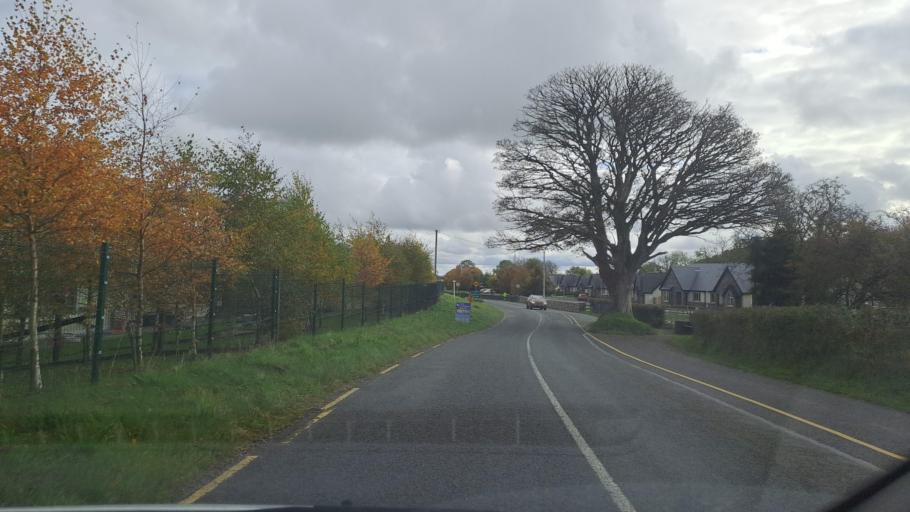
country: IE
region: Ulster
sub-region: An Cabhan
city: Mullagh
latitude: 53.8138
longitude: -6.9609
